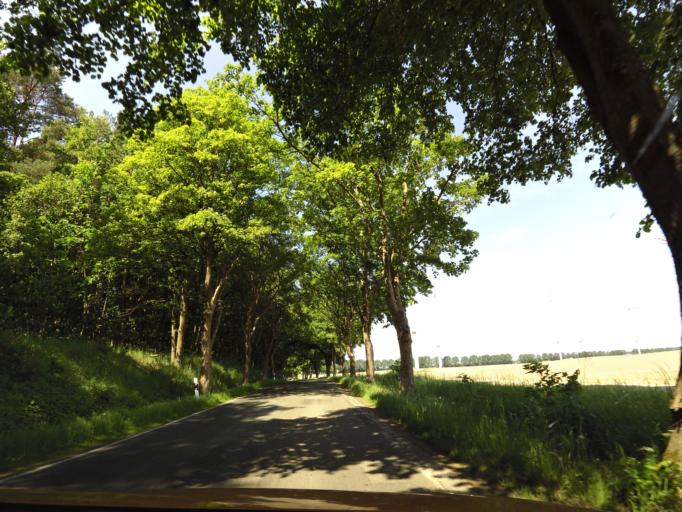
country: DE
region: Mecklenburg-Vorpommern
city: Neuburg
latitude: 53.4108
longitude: 11.8950
